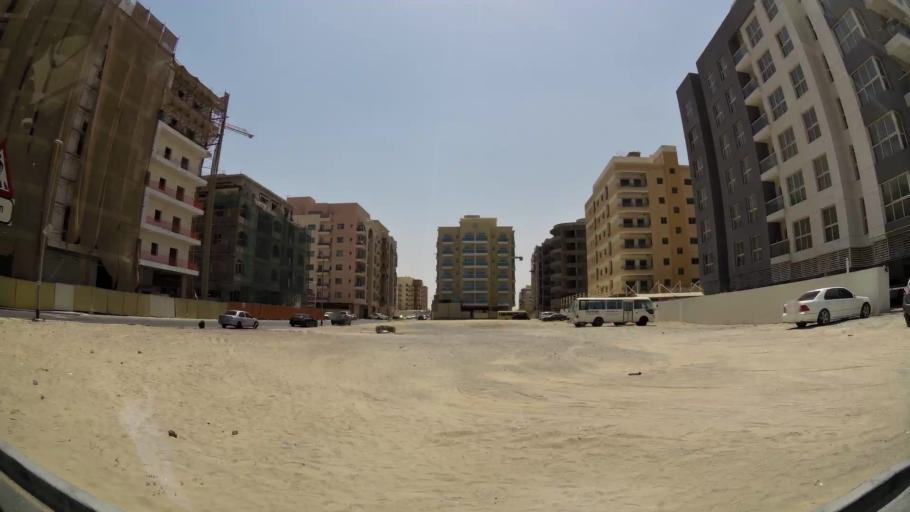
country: AE
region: Ash Shariqah
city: Sharjah
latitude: 25.1867
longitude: 55.4044
